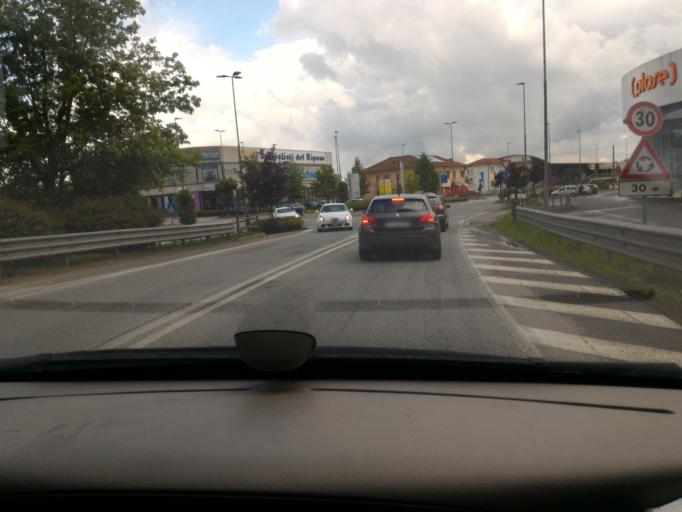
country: IT
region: Piedmont
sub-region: Provincia di Cuneo
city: Savigliano
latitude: 44.6380
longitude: 7.6632
